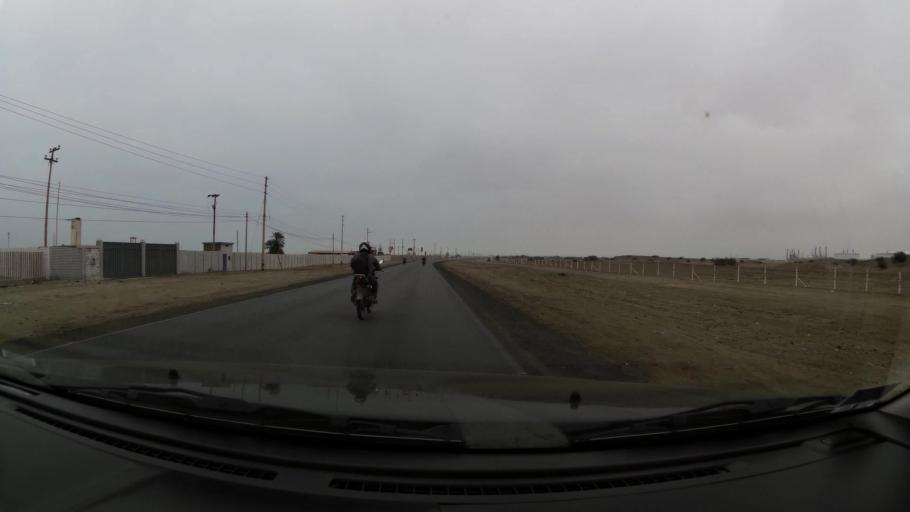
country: PE
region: Ica
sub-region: Provincia de Pisco
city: Pisco
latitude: -13.7775
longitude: -76.2374
